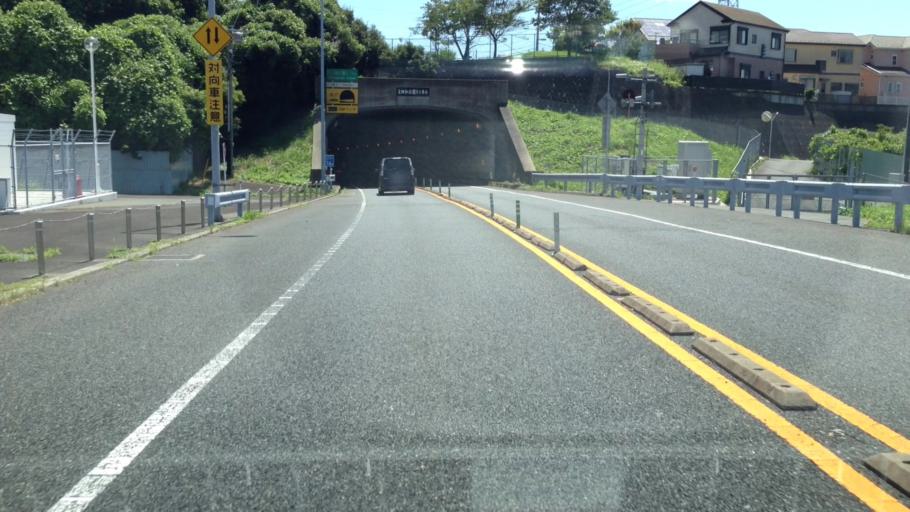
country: JP
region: Kanagawa
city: Yokosuka
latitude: 35.2235
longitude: 139.6369
